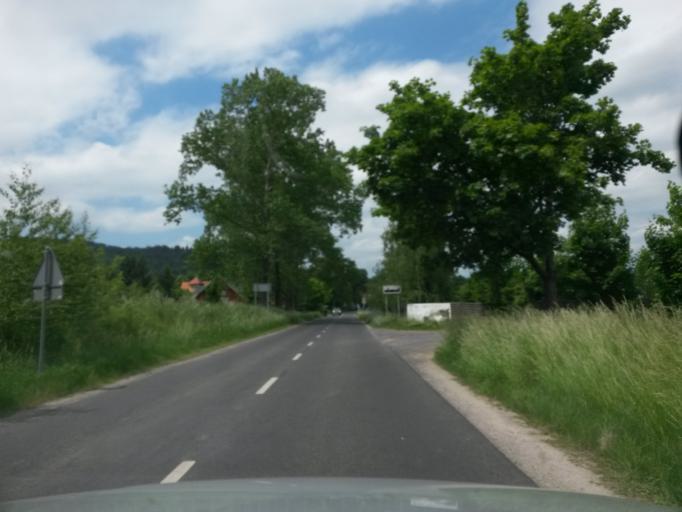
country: PL
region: Lower Silesian Voivodeship
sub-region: Powiat jeleniogorski
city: Podgorzyn
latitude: 50.8427
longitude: 15.6469
